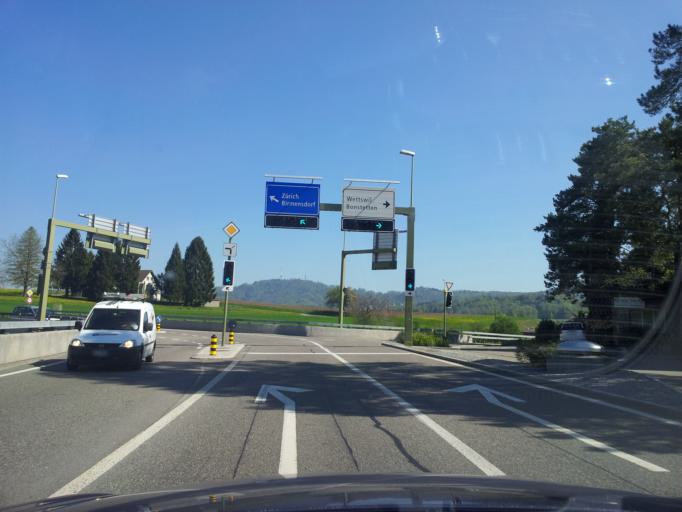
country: CH
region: Zurich
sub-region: Bezirk Affoltern
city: Bonstetten
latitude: 47.3163
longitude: 8.4598
